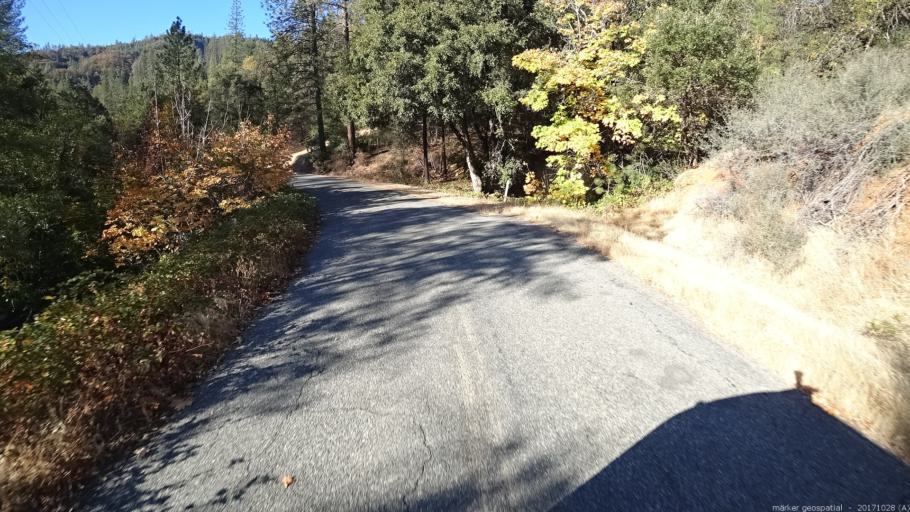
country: US
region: California
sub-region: Trinity County
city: Lewiston
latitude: 40.6542
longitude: -122.6668
